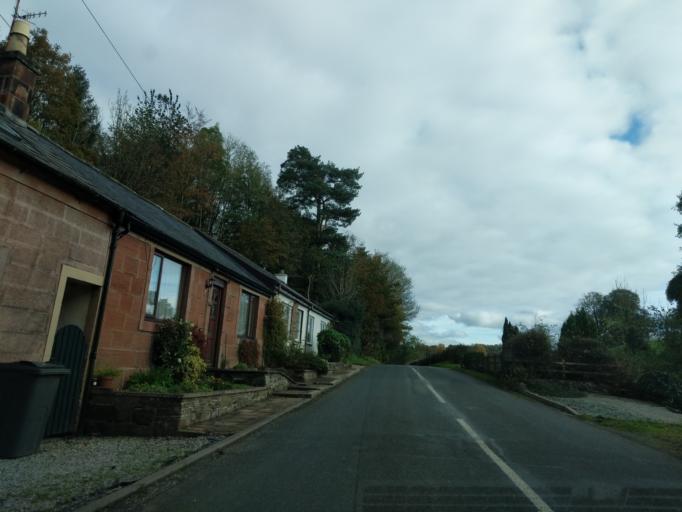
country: GB
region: Scotland
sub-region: Dumfries and Galloway
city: Thornhill
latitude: 55.2404
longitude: -3.7873
